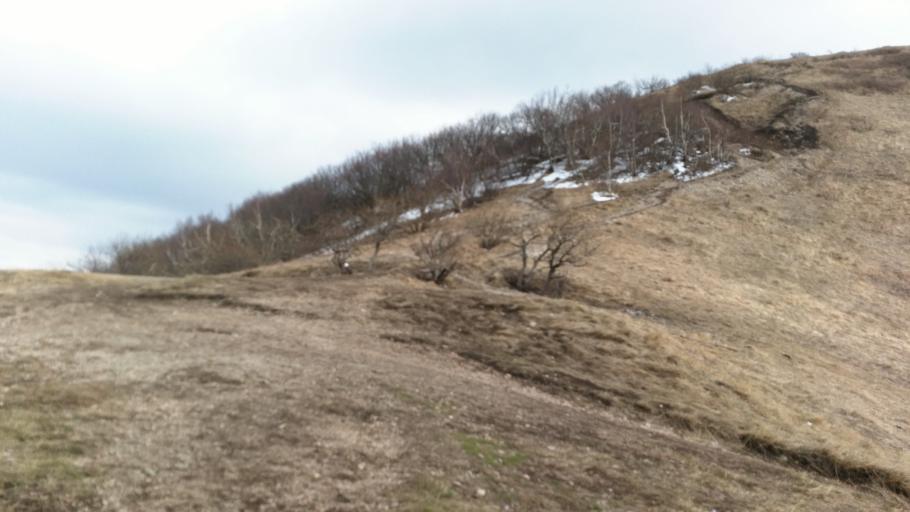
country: RU
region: Stavropol'skiy
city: Zheleznovodsk
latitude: 44.1036
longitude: 43.0205
